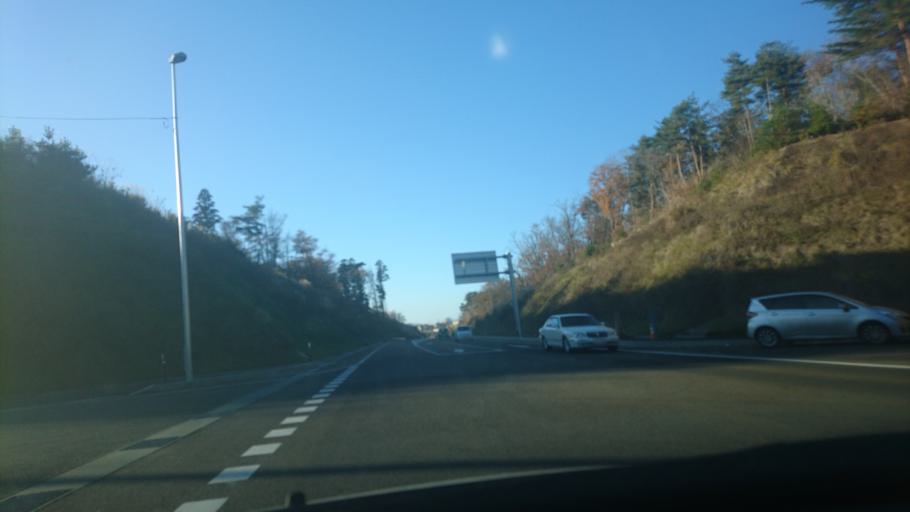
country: JP
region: Iwate
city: Ichinoseki
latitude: 38.9047
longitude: 141.1735
